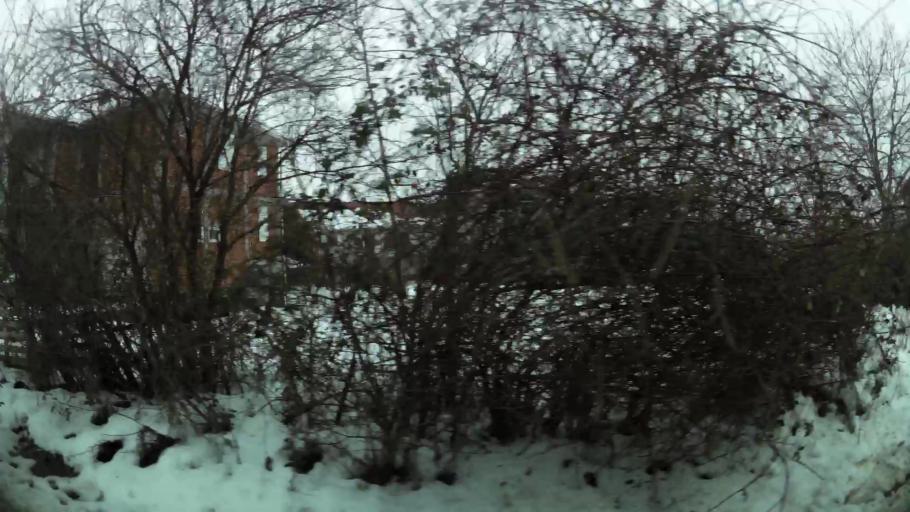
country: RS
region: Central Serbia
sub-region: Belgrade
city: Zvezdara
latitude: 44.7462
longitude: 20.5157
